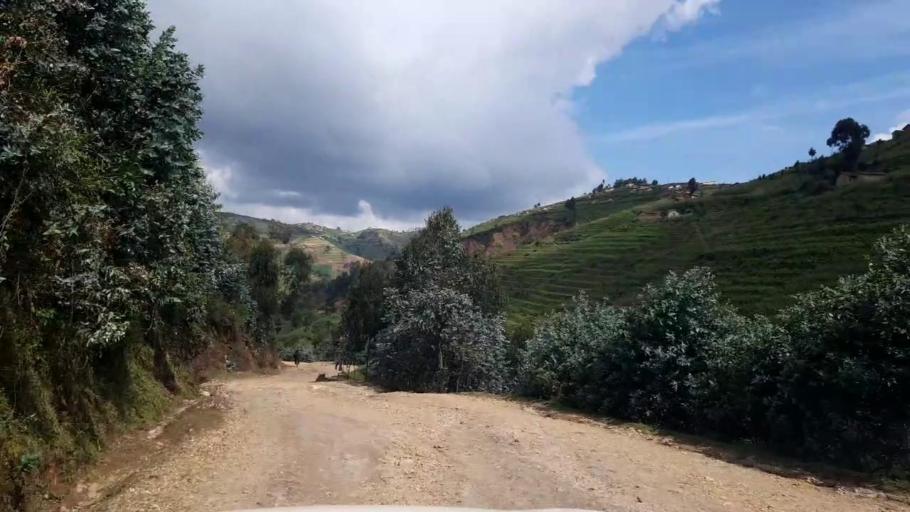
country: RW
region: Western Province
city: Kibuye
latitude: -1.8927
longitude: 29.4611
